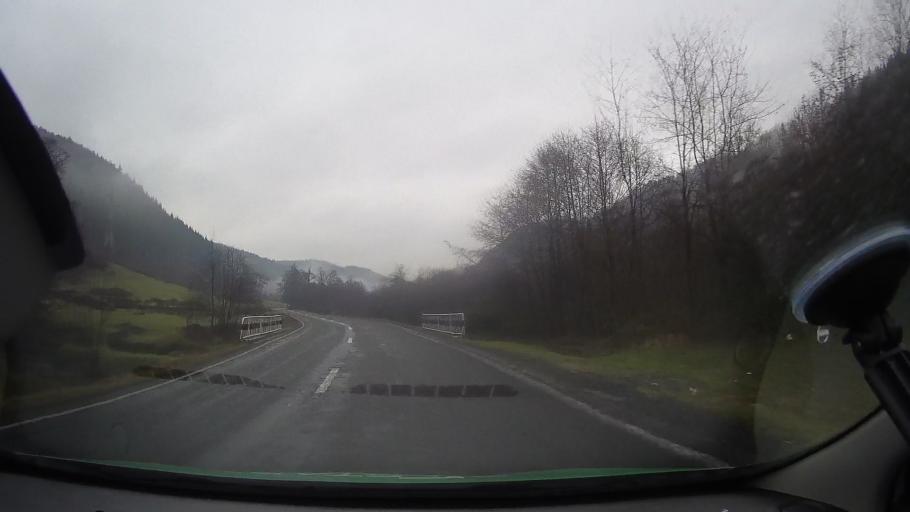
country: RO
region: Arad
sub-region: Comuna Plescuta
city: Plescuta
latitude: 46.3077
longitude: 22.4566
